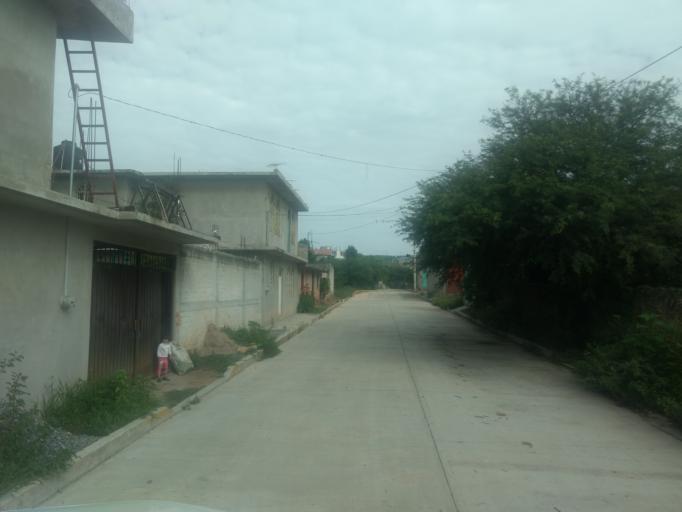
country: MX
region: Oaxaca
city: Ciudad de Huajuapam de Leon
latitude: 17.8042
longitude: -97.7910
